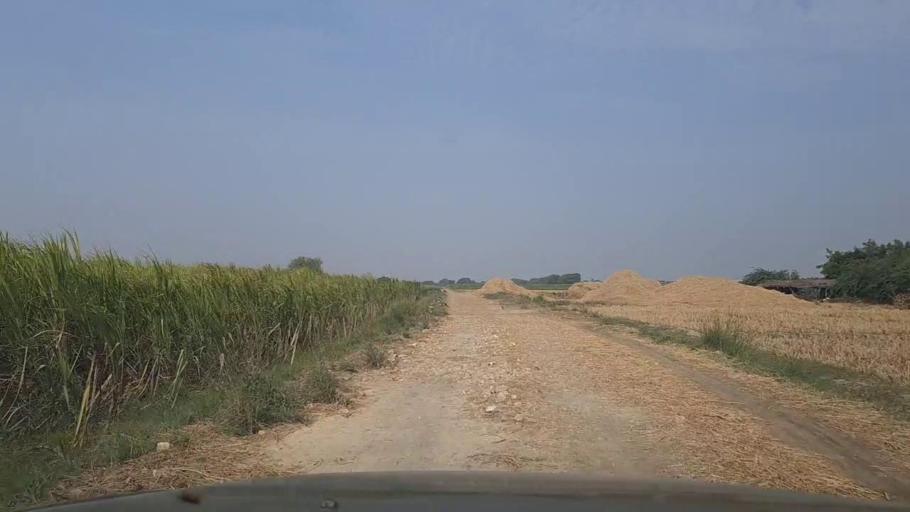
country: PK
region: Sindh
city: Bulri
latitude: 25.0158
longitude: 68.2838
